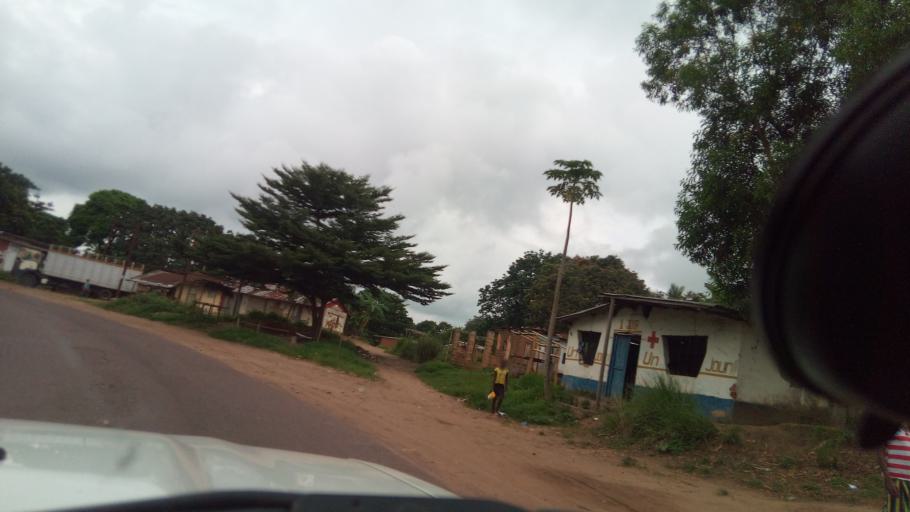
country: CD
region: Bas-Congo
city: Kasangulu
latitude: -4.9045
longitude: 15.1627
